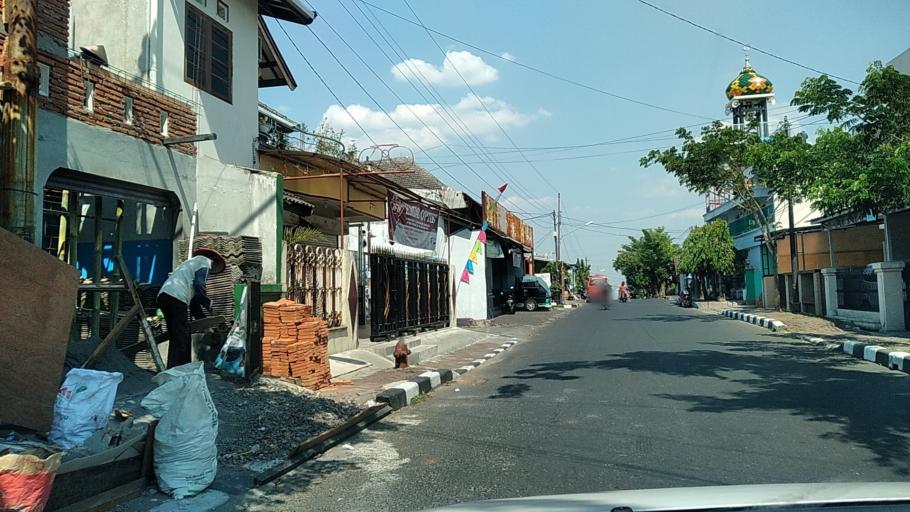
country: ID
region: Central Java
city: Ungaran
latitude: -7.0714
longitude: 110.4299
